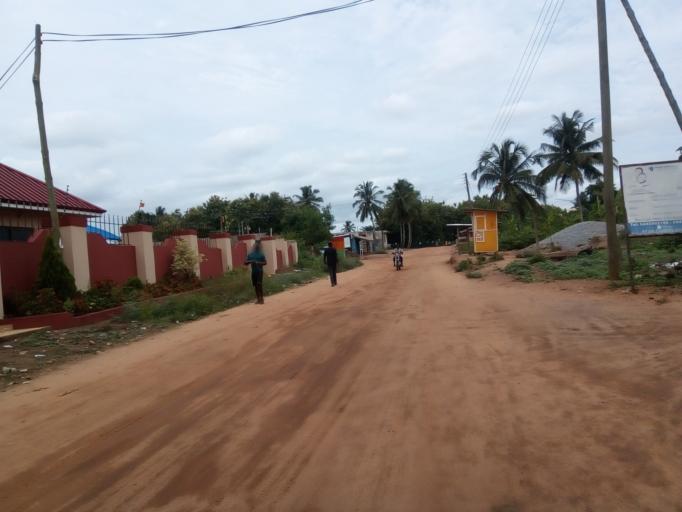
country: GH
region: Eastern
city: Nsawam
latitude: 5.7786
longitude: -0.3388
